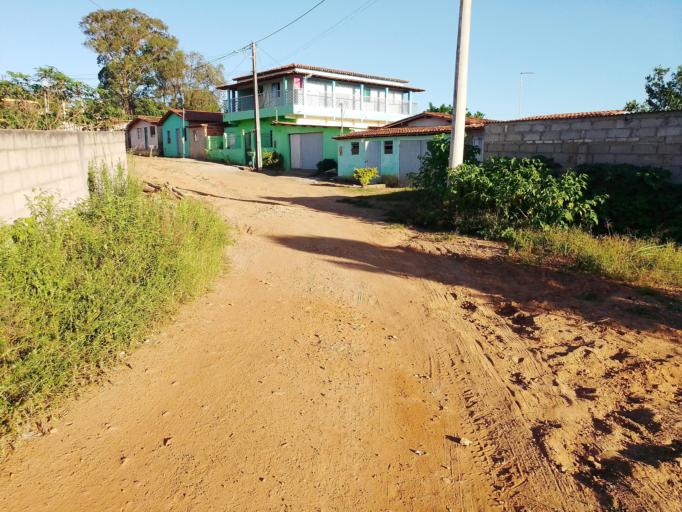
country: BR
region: Bahia
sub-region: Pocoes
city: Pocoes
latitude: -14.7513
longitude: -40.5126
